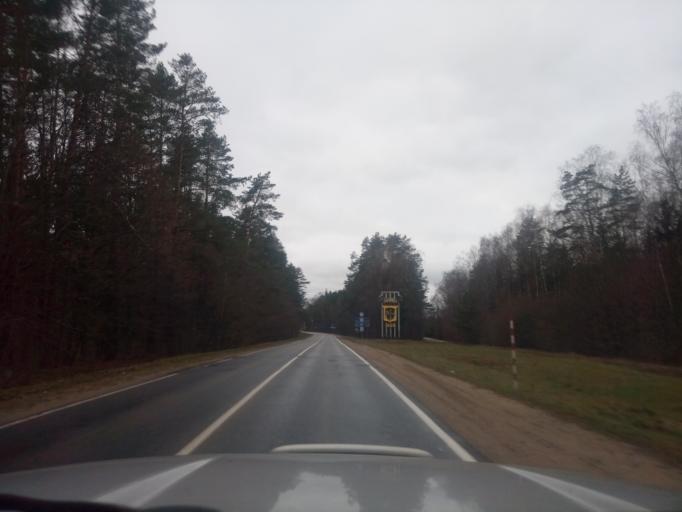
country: BY
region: Minsk
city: Kapyl'
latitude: 53.1594
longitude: 27.1100
